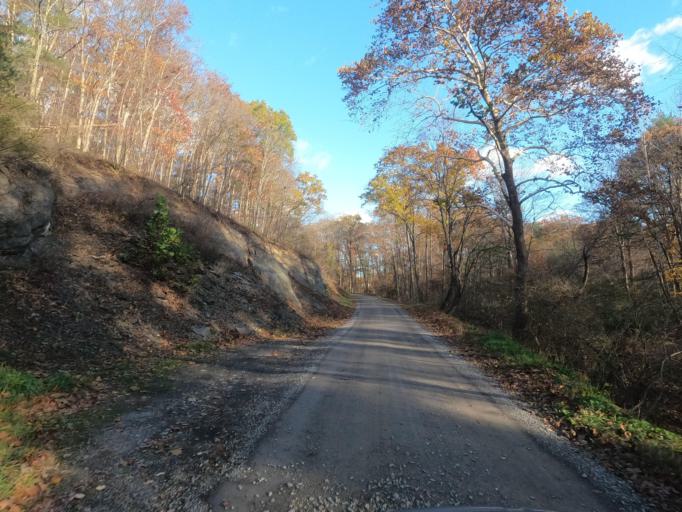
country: US
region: West Virginia
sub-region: Morgan County
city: Berkeley Springs
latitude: 39.6701
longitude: -78.4593
